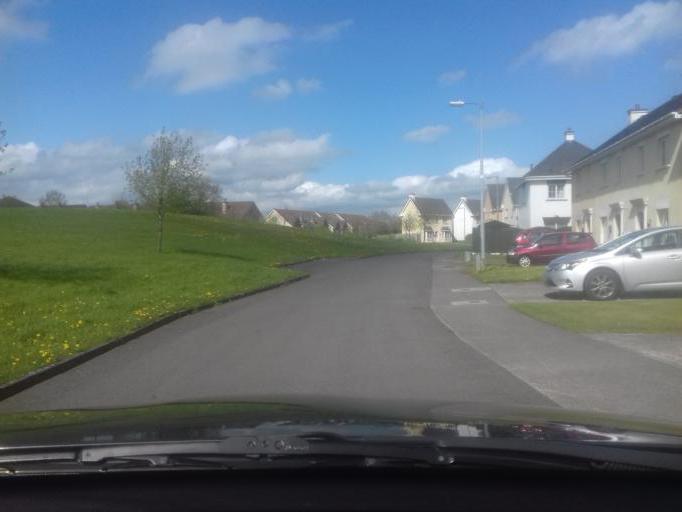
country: IE
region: Leinster
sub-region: Laois
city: Portlaoise
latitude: 53.0475
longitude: -7.2709
